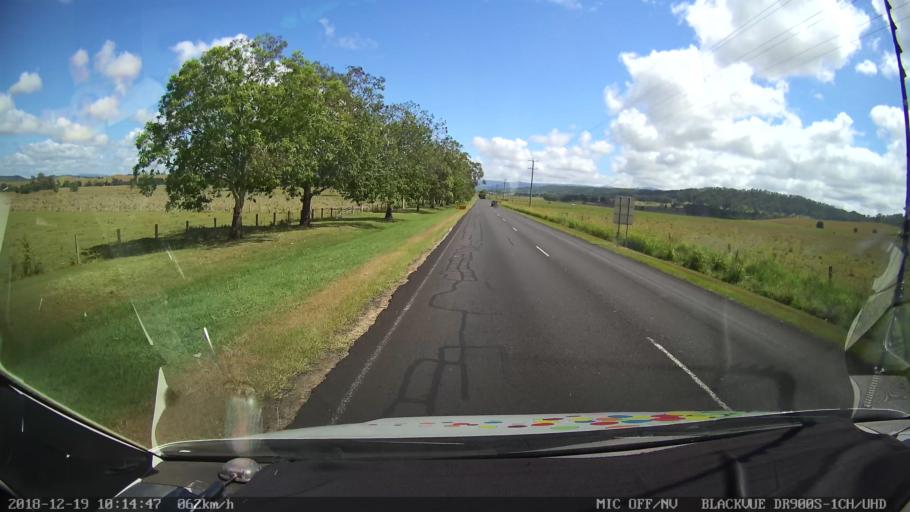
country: AU
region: New South Wales
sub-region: Kyogle
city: Kyogle
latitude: -28.6112
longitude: 153.0099
